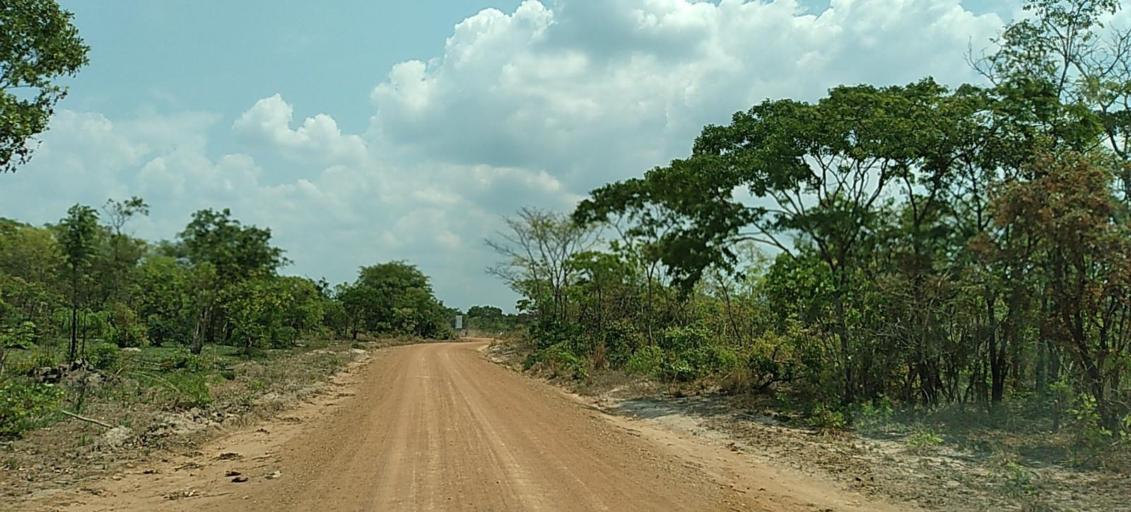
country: ZM
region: Copperbelt
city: Luanshya
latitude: -13.1522
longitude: 28.3146
